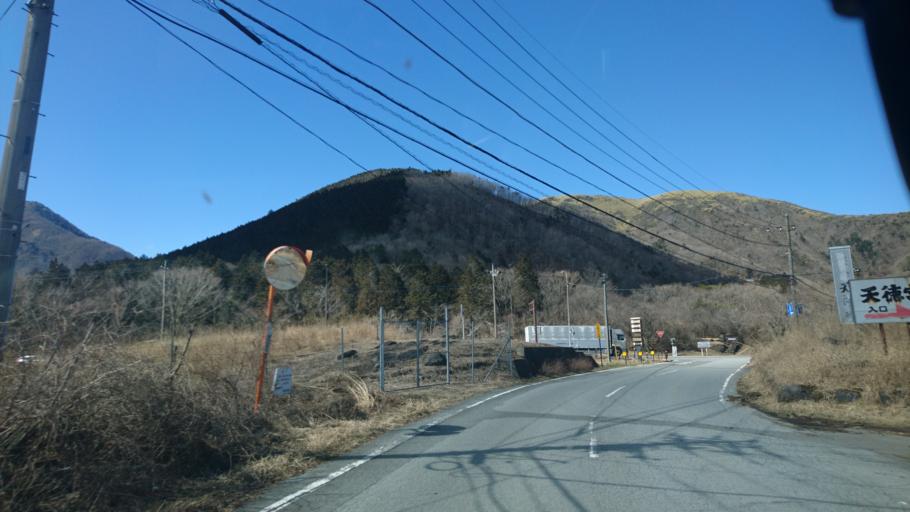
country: JP
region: Yamanashi
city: Fujikawaguchiko
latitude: 35.4324
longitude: 138.5977
